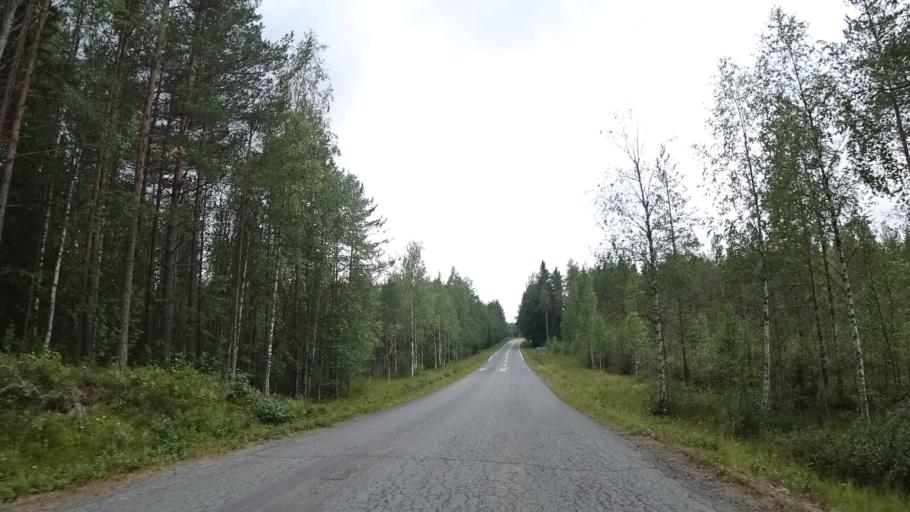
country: FI
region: North Karelia
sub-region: Joensuu
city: Ilomantsi
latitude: 62.9394
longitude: 31.2870
